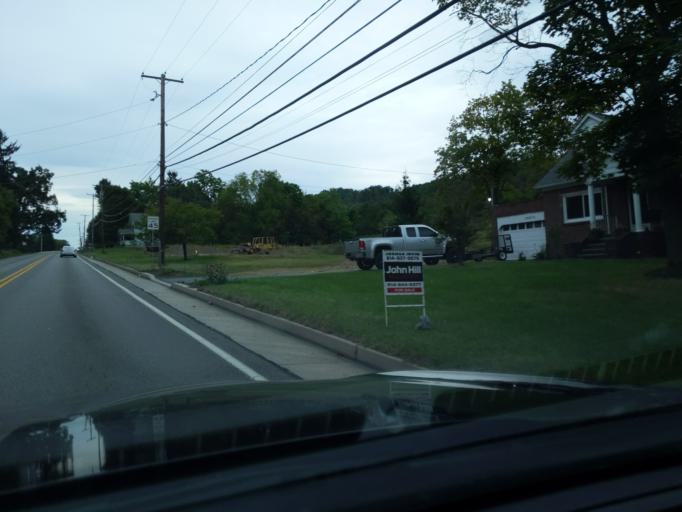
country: US
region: Pennsylvania
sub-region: Blair County
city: Duncansville
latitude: 40.3986
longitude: -78.4360
